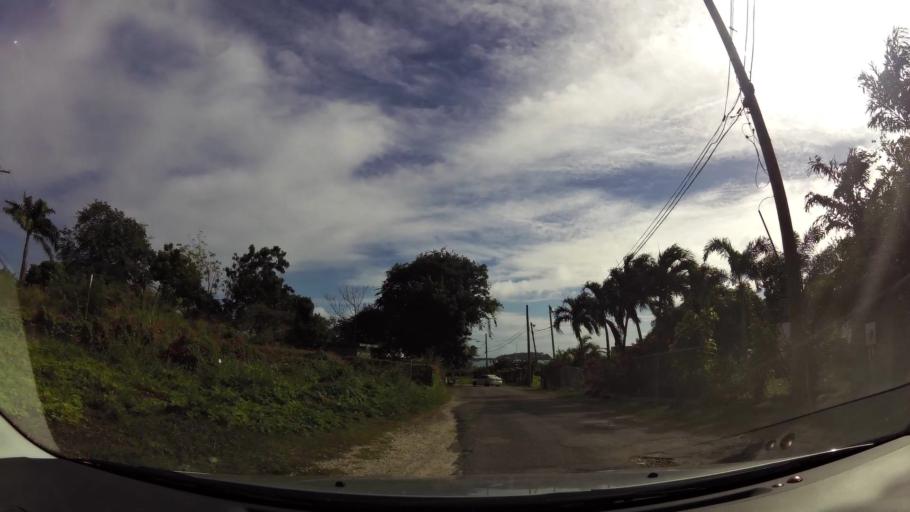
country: AG
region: Saint Paul
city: Falmouth
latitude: 17.0252
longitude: -61.7801
